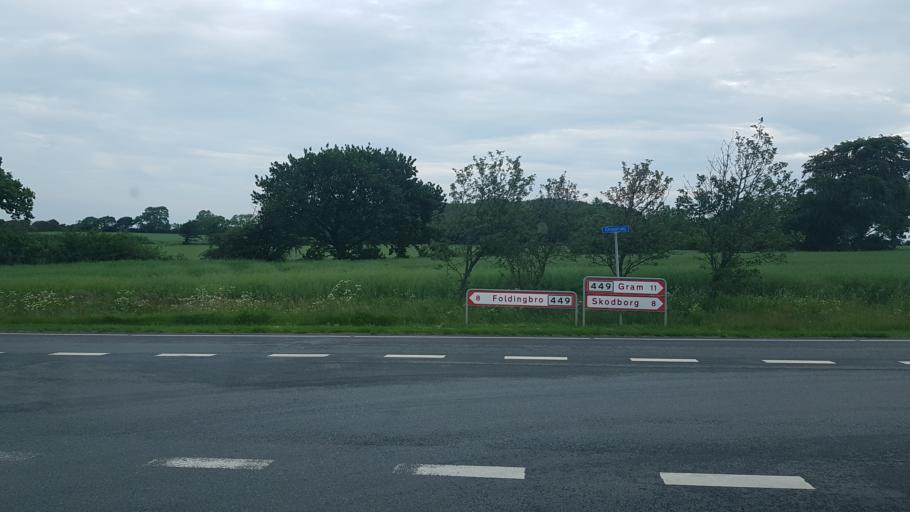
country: DK
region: South Denmark
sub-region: Vejen Kommune
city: Rodding
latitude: 55.3768
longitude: 9.0610
